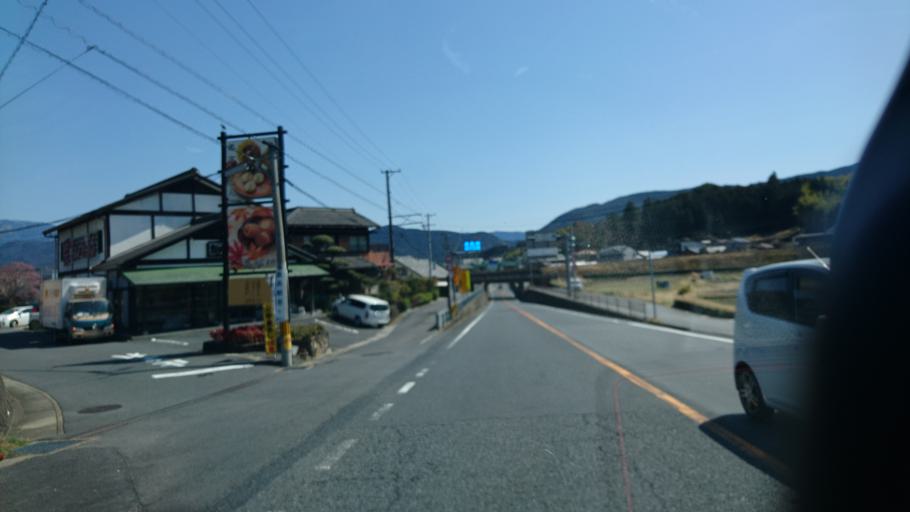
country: JP
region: Gifu
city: Nakatsugawa
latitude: 35.4541
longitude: 137.3981
